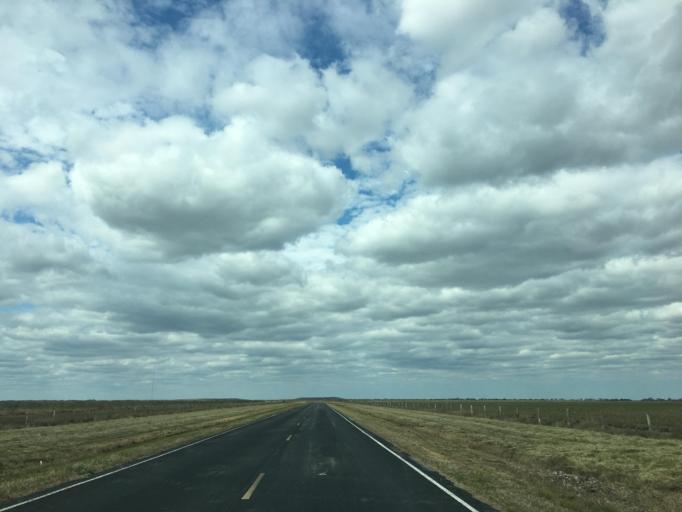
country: US
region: Texas
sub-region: Brazoria County
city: Oyster Creek
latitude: 29.0636
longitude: -95.2899
